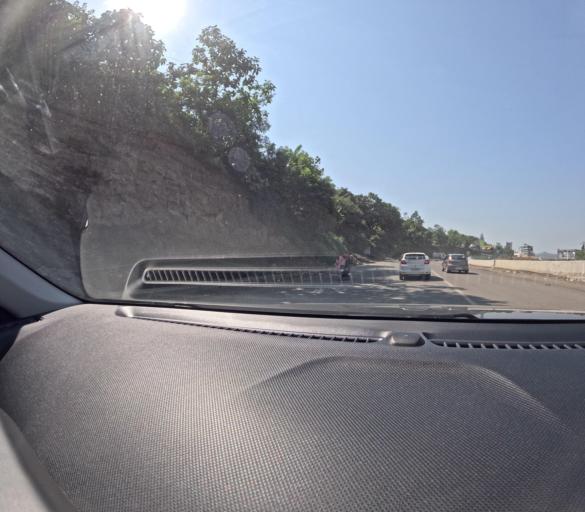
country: IN
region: Maharashtra
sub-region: Pune Division
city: Kharakvasla
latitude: 18.5062
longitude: 73.7868
